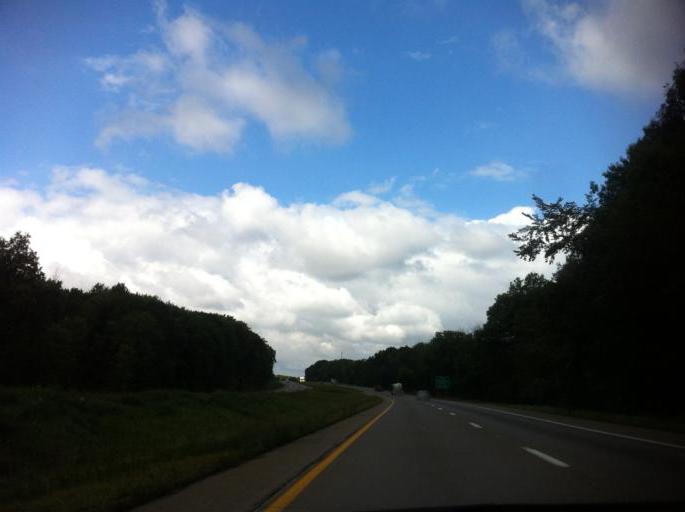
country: US
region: Pennsylvania
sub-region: Mercer County
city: Hermitage
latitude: 41.1835
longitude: -80.4019
